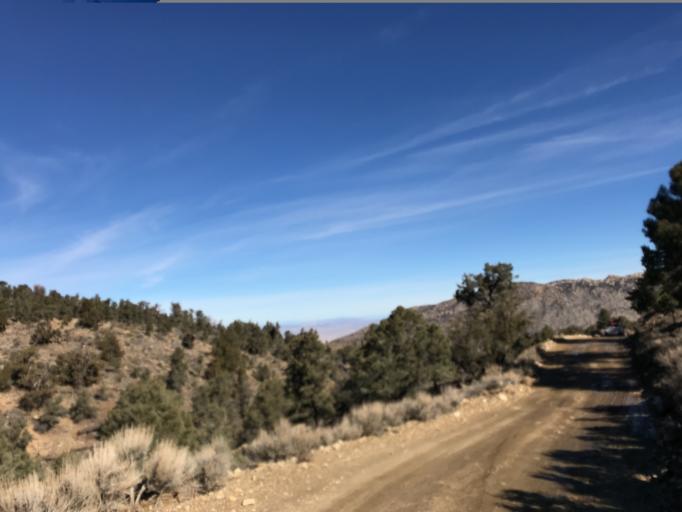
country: US
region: California
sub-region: San Bernardino County
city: Big Bear City
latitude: 34.2727
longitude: -116.7787
